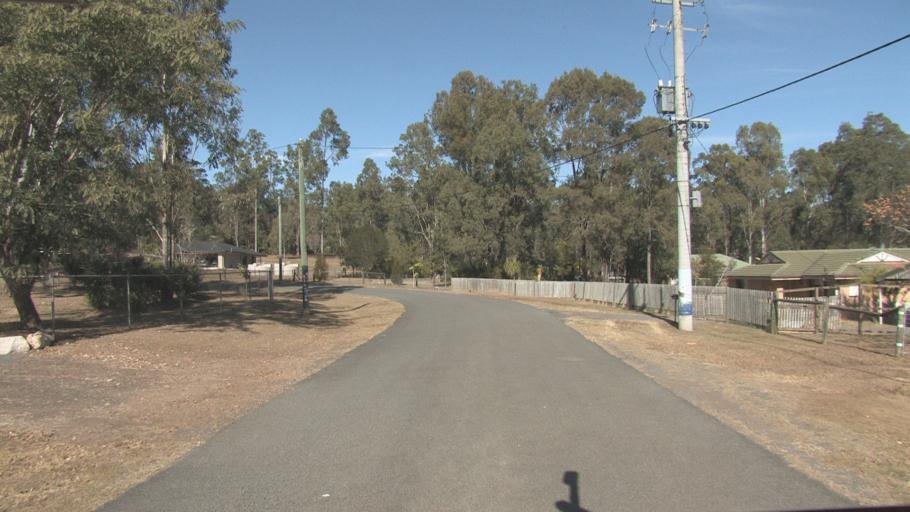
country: AU
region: Queensland
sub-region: Logan
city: Cedar Vale
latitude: -27.8589
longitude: 152.9826
